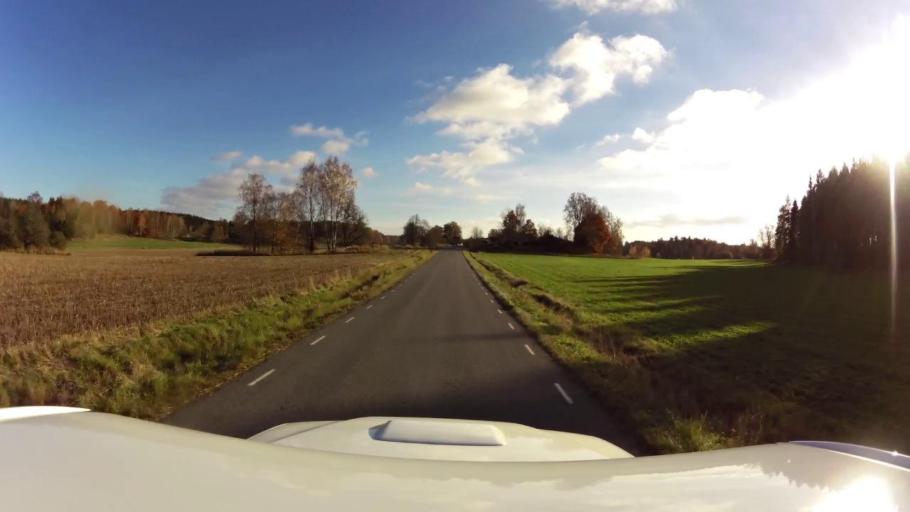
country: SE
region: OEstergoetland
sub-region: Linkopings Kommun
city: Vikingstad
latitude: 58.2589
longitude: 15.4596
